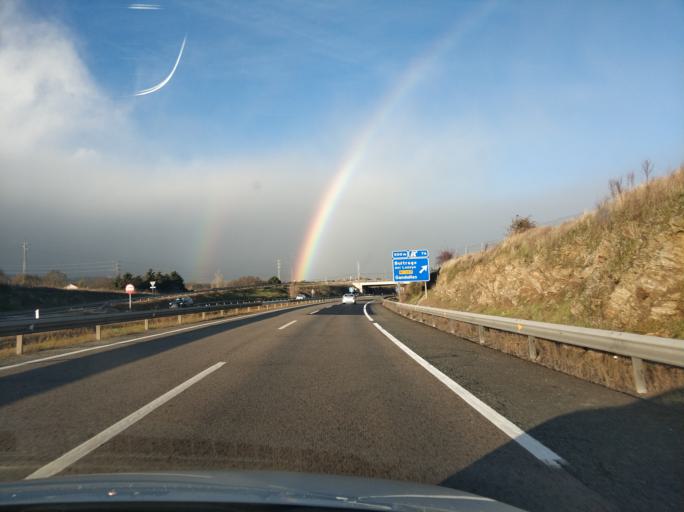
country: ES
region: Madrid
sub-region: Provincia de Madrid
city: Buitrago del Lozoya
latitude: 40.9963
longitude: -3.6416
